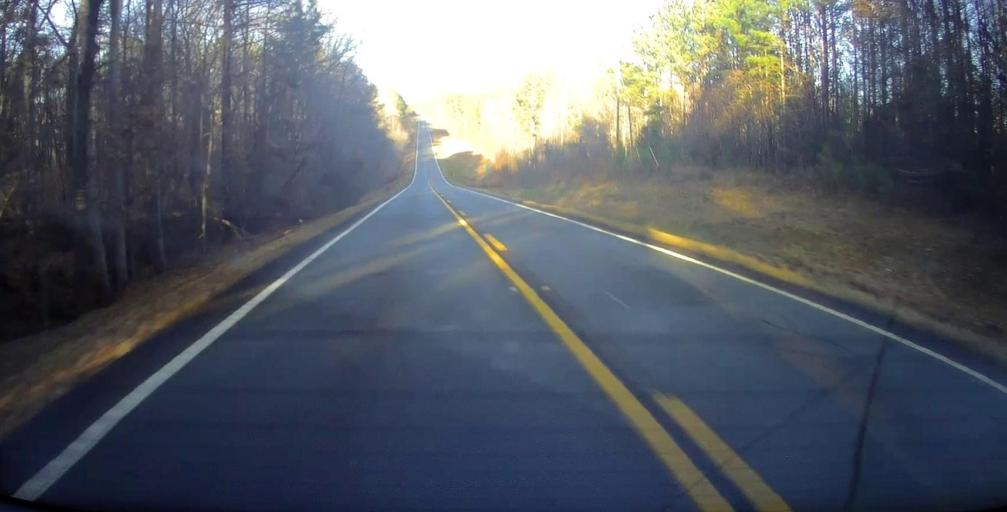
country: US
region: Georgia
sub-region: Meriwether County
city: Manchester
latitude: 32.8096
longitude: -84.4914
